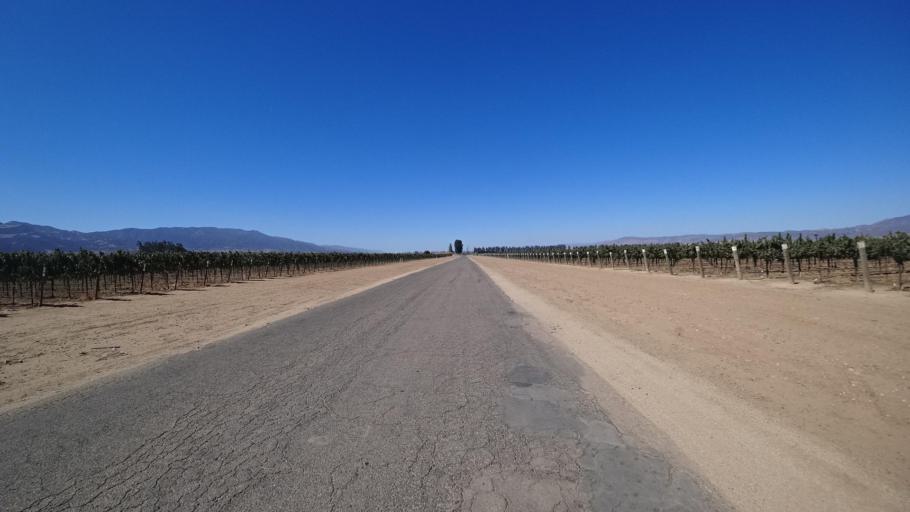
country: US
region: California
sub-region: Monterey County
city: Greenfield
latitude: 36.3186
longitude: -121.2733
